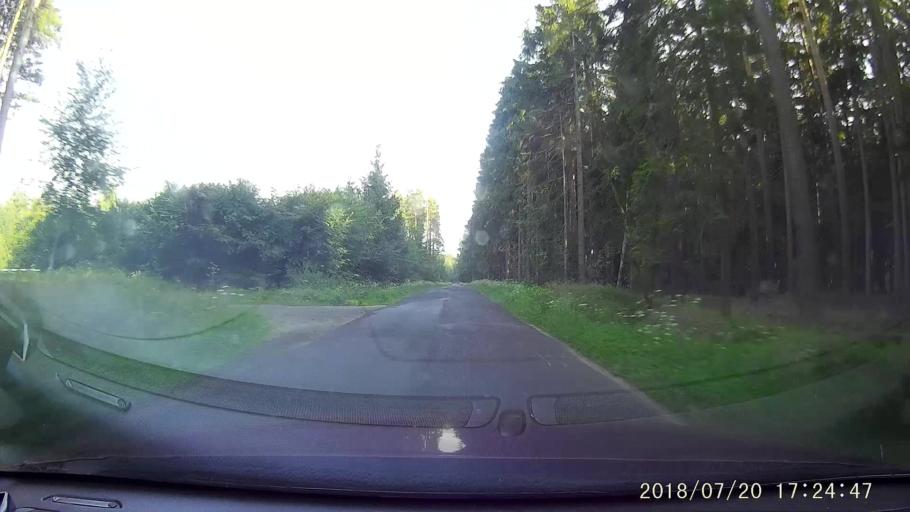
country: PL
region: Lower Silesian Voivodeship
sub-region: Powiat lubanski
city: Lesna
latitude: 50.9672
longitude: 15.2970
